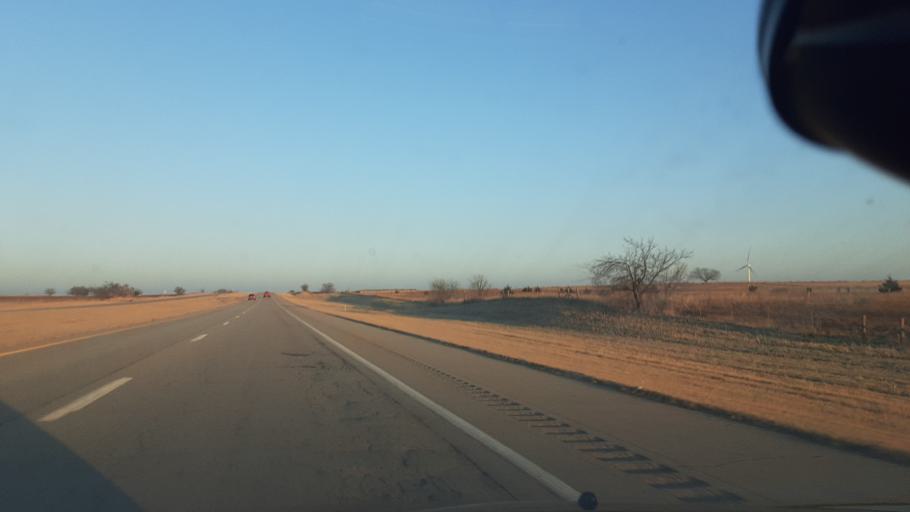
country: US
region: Oklahoma
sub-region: Noble County
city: Perry
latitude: 36.3980
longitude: -97.3845
